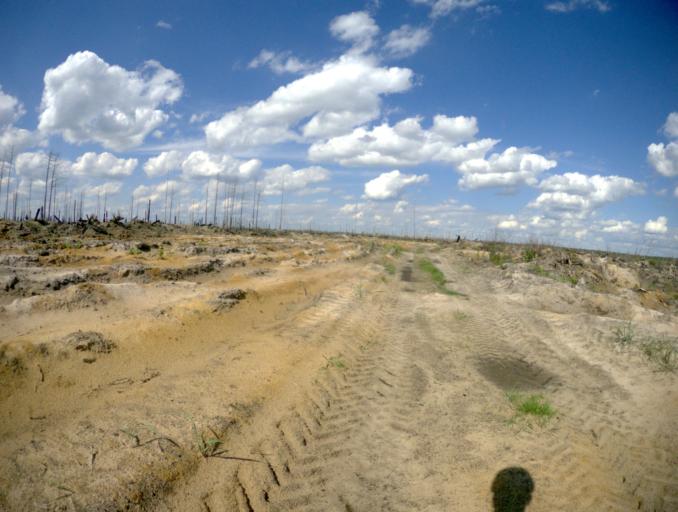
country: RU
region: Vladimir
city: Velikodvorskiy
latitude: 55.3067
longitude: 40.9044
